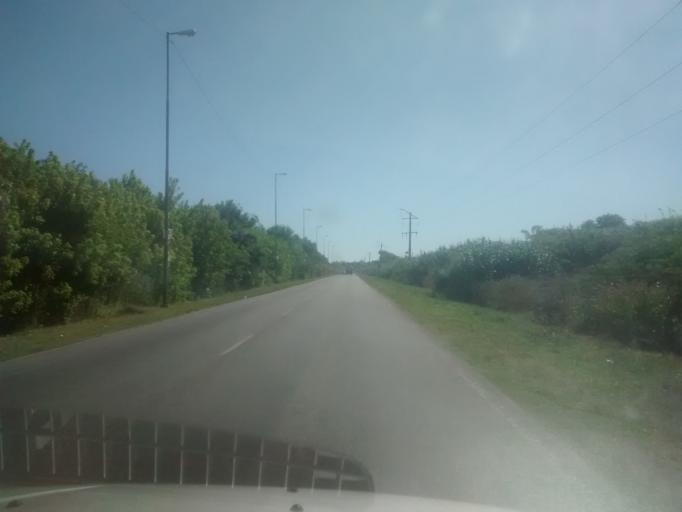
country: AR
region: Buenos Aires
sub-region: Partido de Berisso
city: Berisso
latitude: -34.9056
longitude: -57.9046
